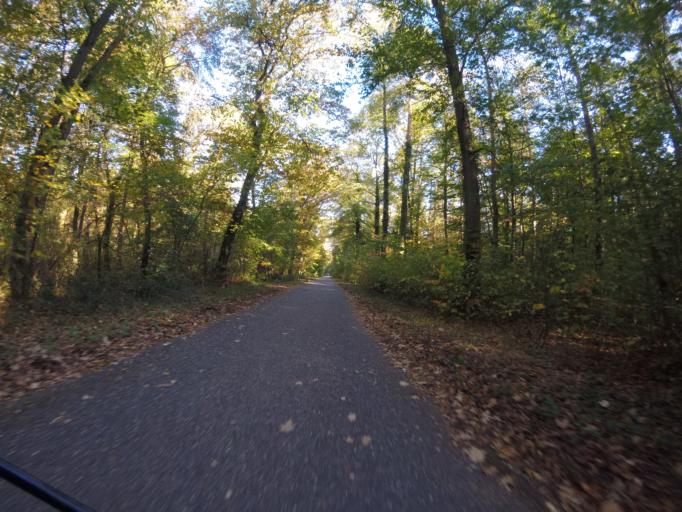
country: DE
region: Baden-Wuerttemberg
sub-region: Karlsruhe Region
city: Eggenstein-Leopoldshafen
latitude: 49.0618
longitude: 8.4094
